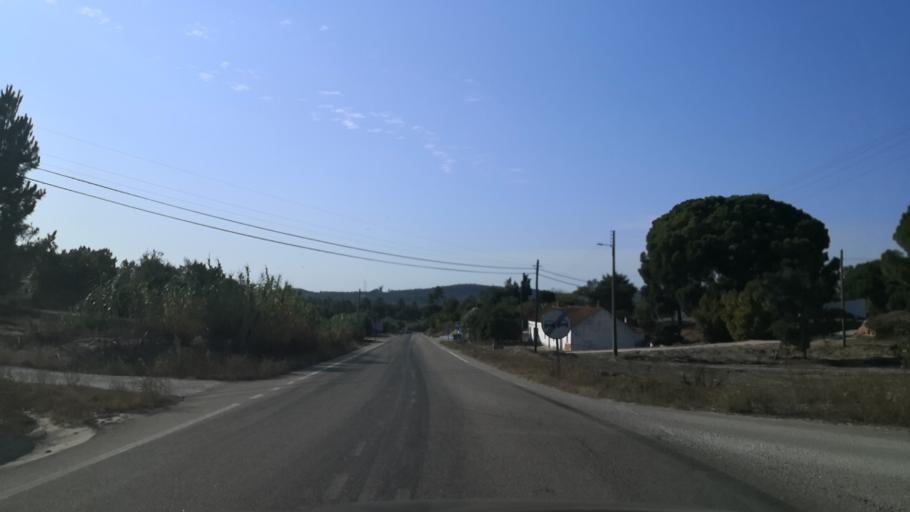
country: PT
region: Santarem
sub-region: Almeirim
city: Fazendas de Almeirim
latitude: 39.1033
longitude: -8.5771
